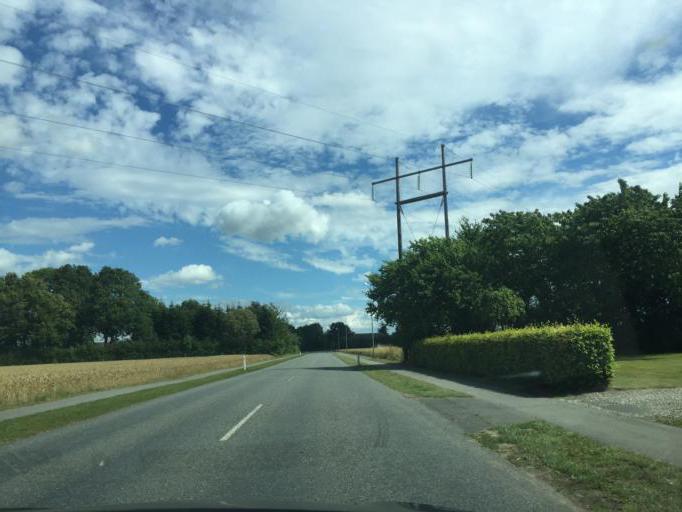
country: DK
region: South Denmark
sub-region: Nordfyns Kommune
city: Otterup
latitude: 55.5199
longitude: 10.3744
